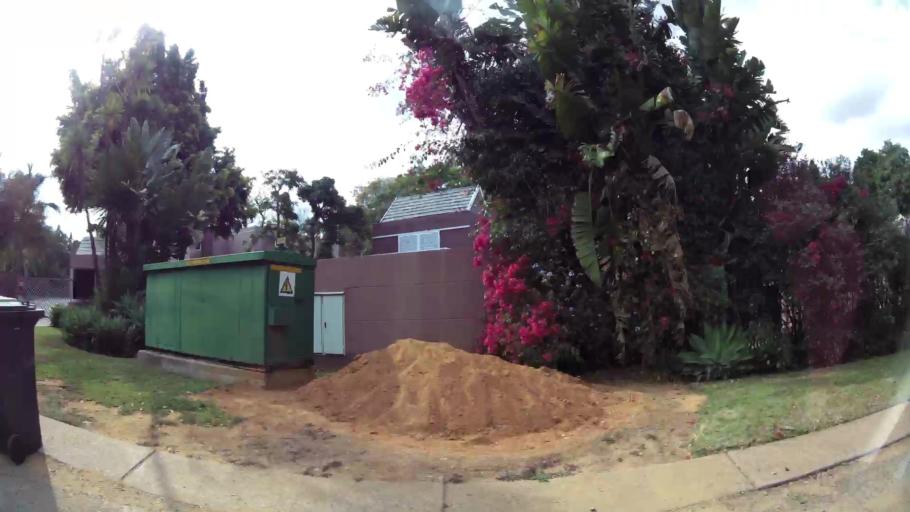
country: ZA
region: Gauteng
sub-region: City of Tshwane Metropolitan Municipality
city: Pretoria
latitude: -25.7593
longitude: 28.3047
